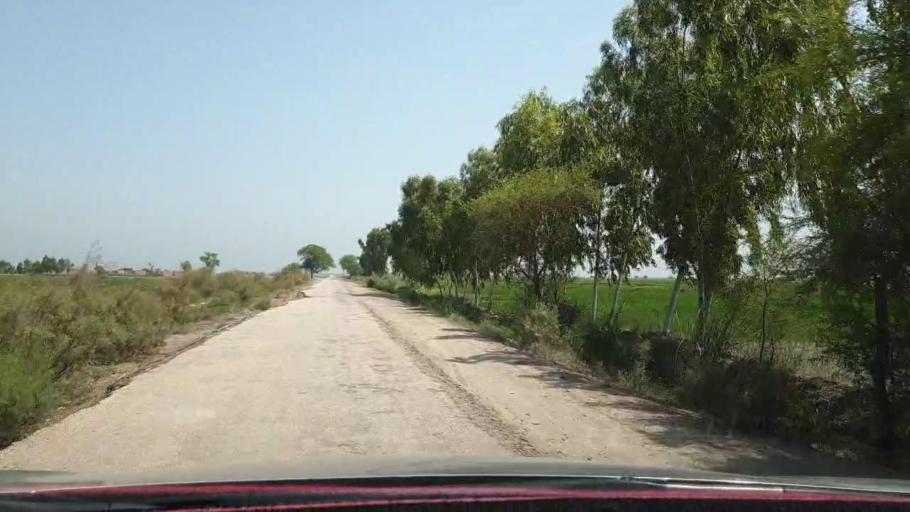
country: PK
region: Sindh
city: Warah
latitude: 27.3815
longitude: 67.7857
